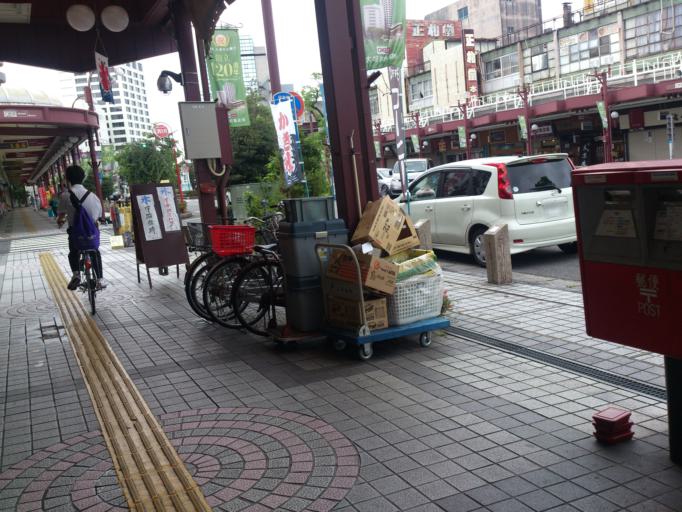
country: JP
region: Gifu
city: Ogaki
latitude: 35.3627
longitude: 136.6174
